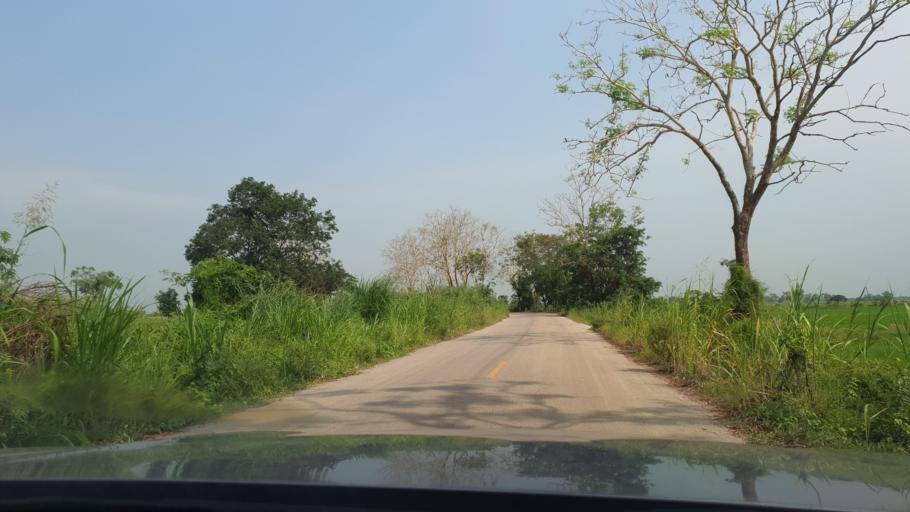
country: TH
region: Phitsanulok
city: Bang Rakam
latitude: 16.8020
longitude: 100.1162
